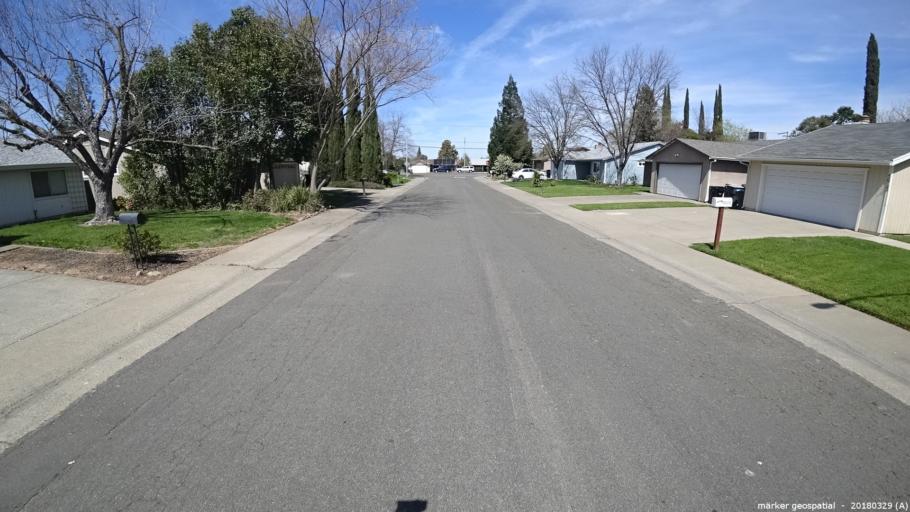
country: US
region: California
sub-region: Sacramento County
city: Rosemont
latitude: 38.5466
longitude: -121.3509
